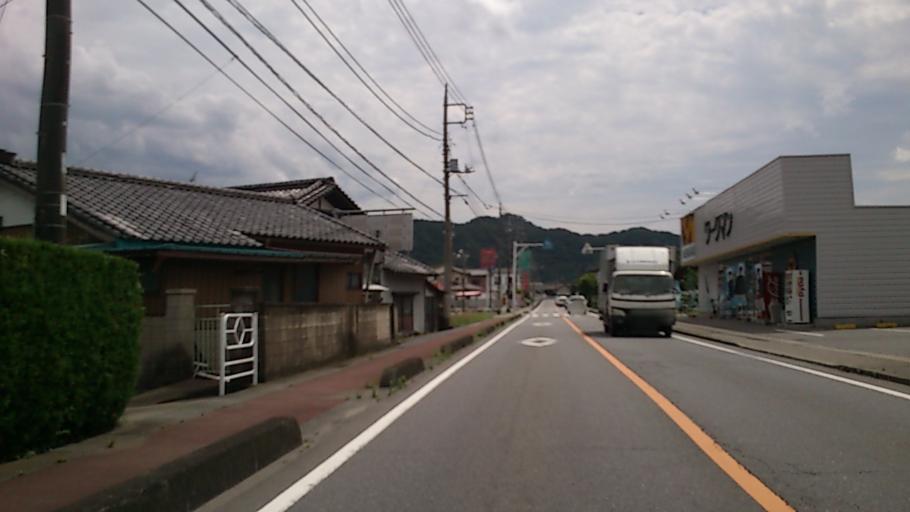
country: JP
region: Gunma
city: Tomioka
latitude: 36.2461
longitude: 138.8583
